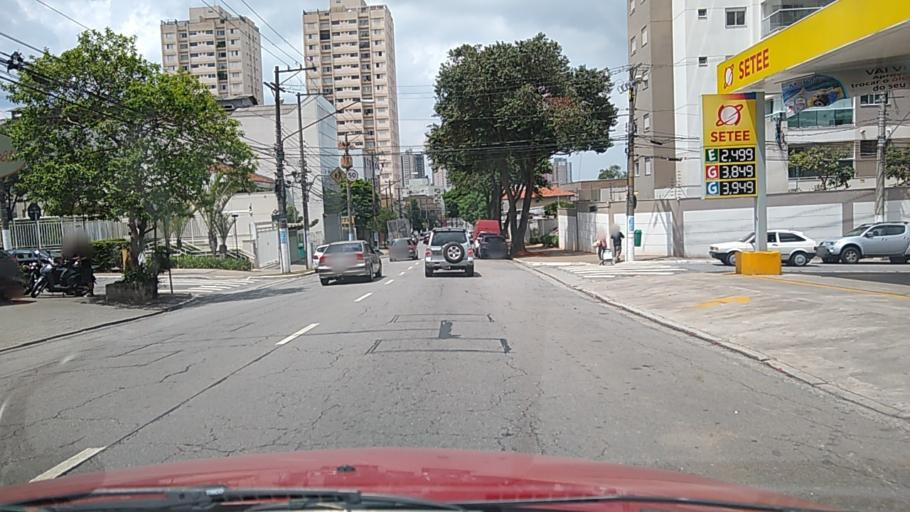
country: BR
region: Sao Paulo
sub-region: Diadema
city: Diadema
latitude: -23.6267
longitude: -46.6339
